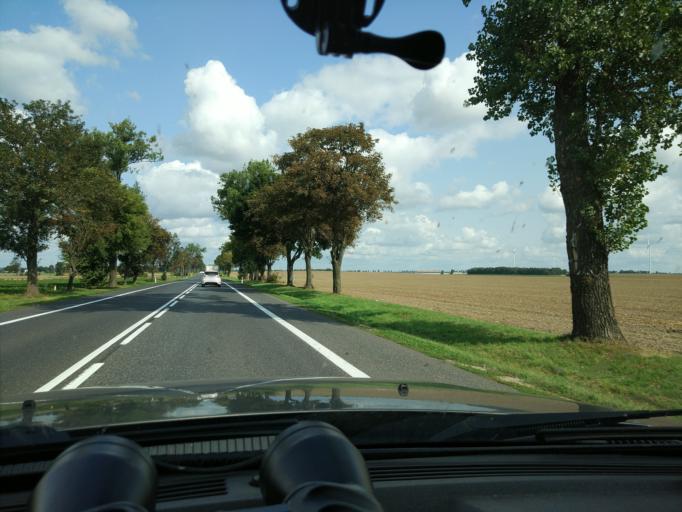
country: PL
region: Masovian Voivodeship
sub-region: Powiat mlawski
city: Wisniewo
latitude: 53.0396
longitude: 20.3405
